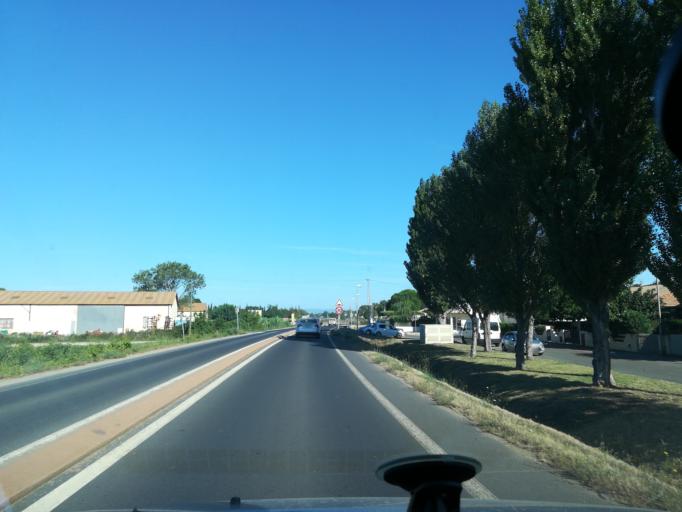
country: FR
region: Languedoc-Roussillon
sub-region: Departement de l'Herault
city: Portiragnes
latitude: 43.3013
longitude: 3.3346
